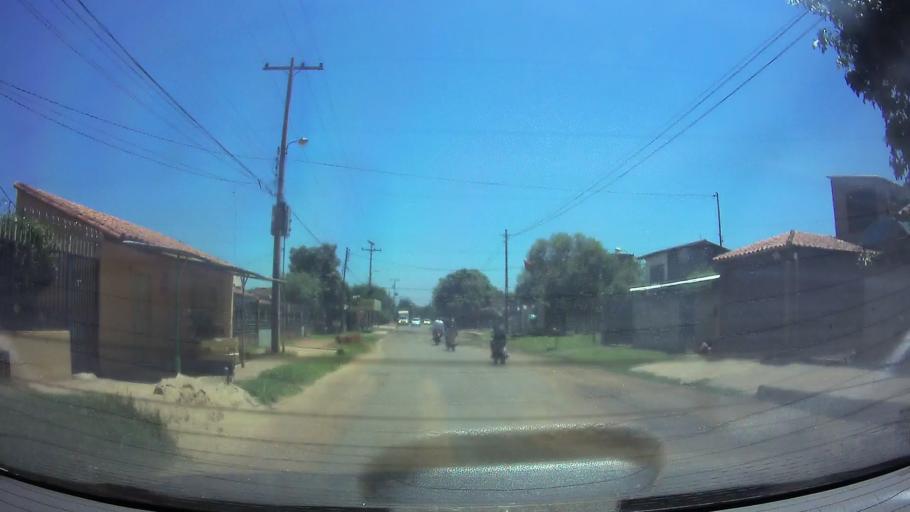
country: PY
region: Central
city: San Lorenzo
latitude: -25.3285
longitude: -57.4858
